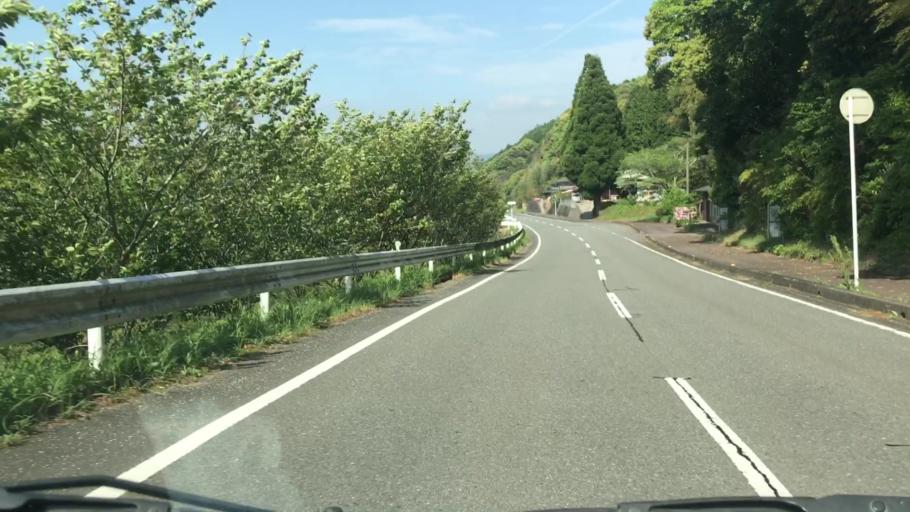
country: JP
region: Saga Prefecture
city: Takeocho-takeo
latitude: 33.2152
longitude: 129.9964
